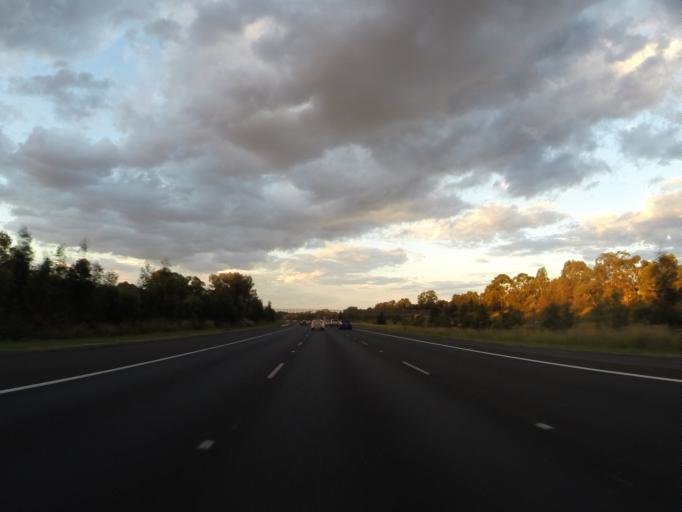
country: AU
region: New South Wales
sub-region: Campbelltown Municipality
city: Leumeah
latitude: -34.0478
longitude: 150.8168
